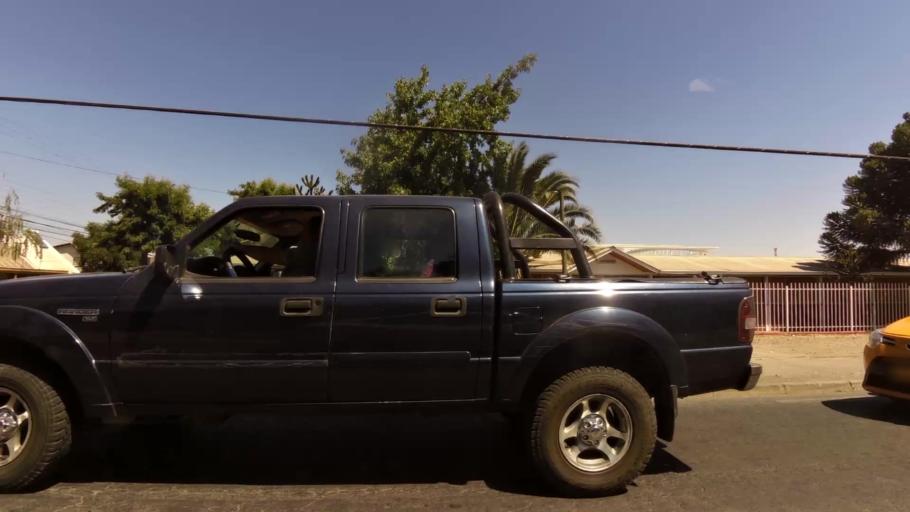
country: CL
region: Maule
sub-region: Provincia de Curico
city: Curico
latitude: -34.9667
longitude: -71.2299
